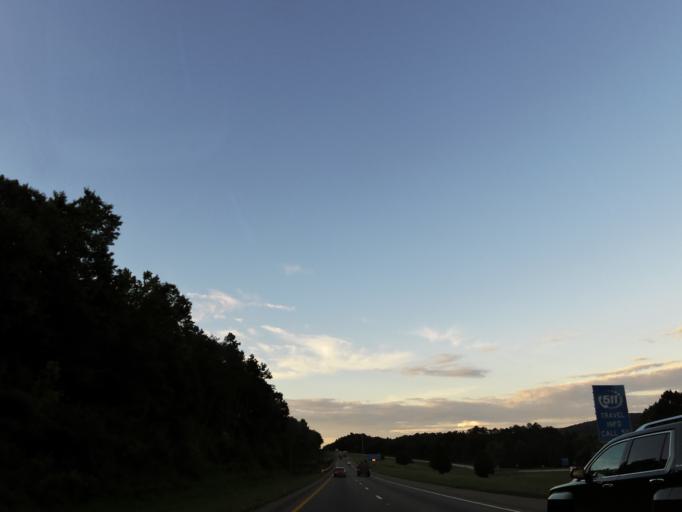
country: US
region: Tennessee
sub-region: McMinn County
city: Athens
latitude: 35.3895
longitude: -84.7206
